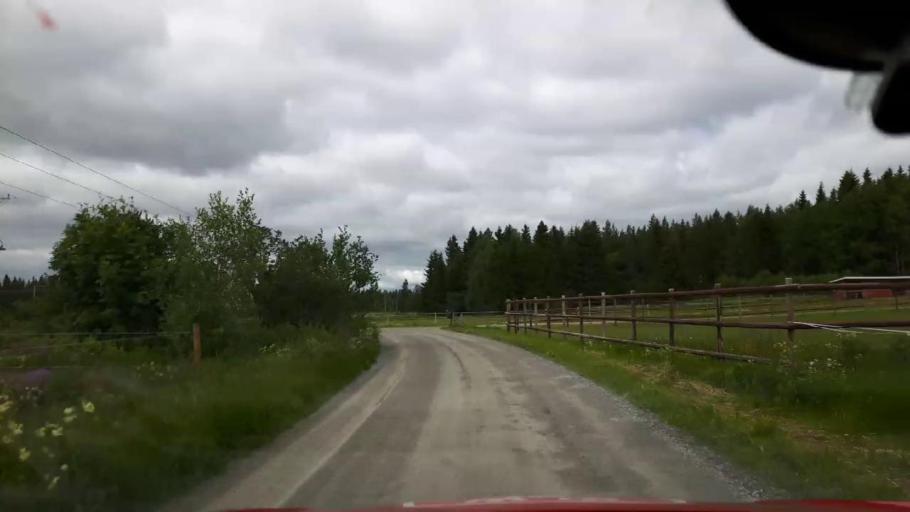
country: SE
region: Jaemtland
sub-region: OEstersunds Kommun
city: Brunflo
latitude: 63.0944
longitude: 14.8219
